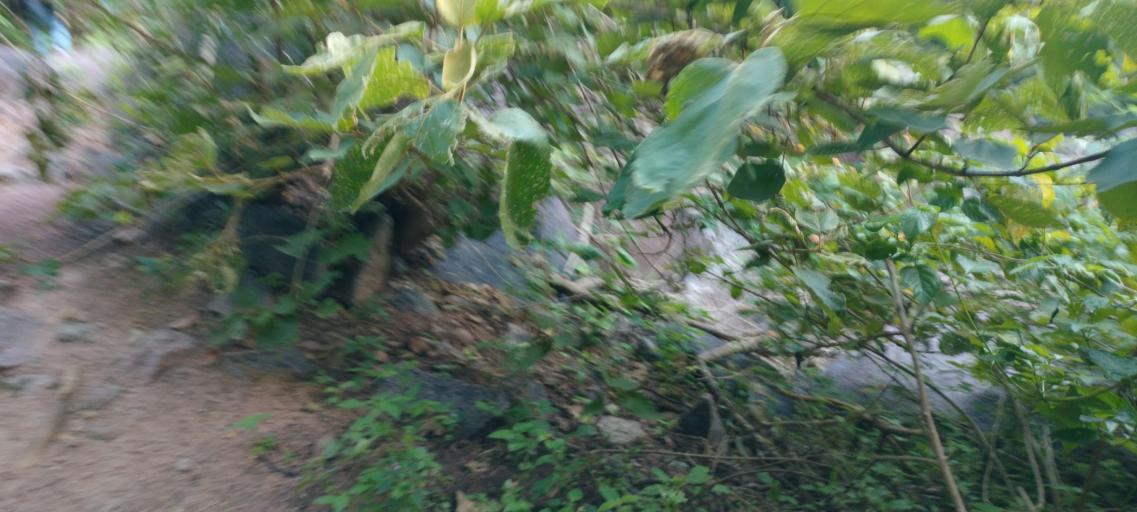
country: IN
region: Telangana
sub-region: Mahbubnagar
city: Farrukhnagar
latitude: 16.8929
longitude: 78.4917
